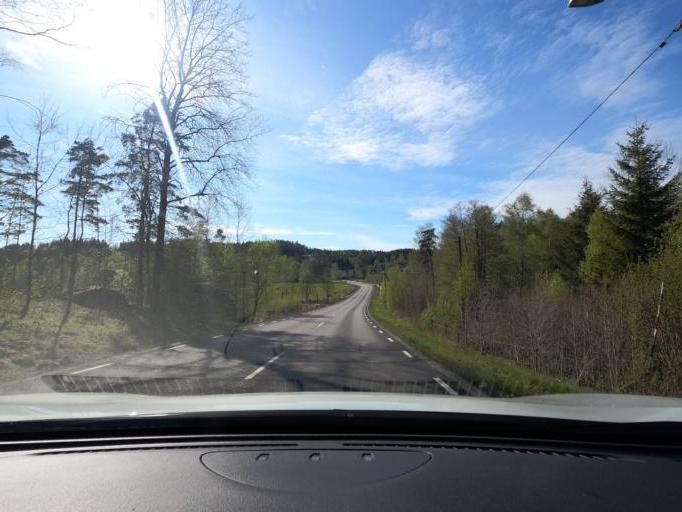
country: SE
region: Vaestra Goetaland
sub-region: Harryda Kommun
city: Landvetter
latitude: 57.6159
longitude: 12.2890
